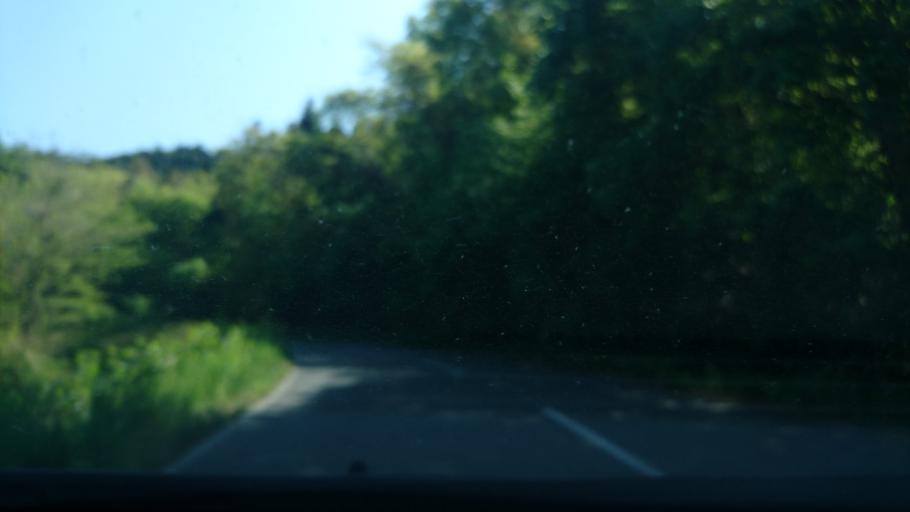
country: JP
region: Iwate
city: Ichinoseki
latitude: 38.9401
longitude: 141.2743
